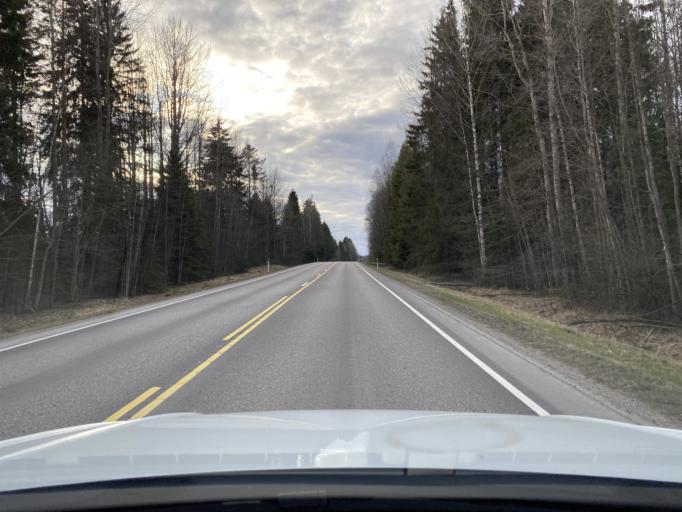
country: FI
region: Haeme
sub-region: Haemeenlinna
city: Renko
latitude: 60.7912
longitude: 24.1190
